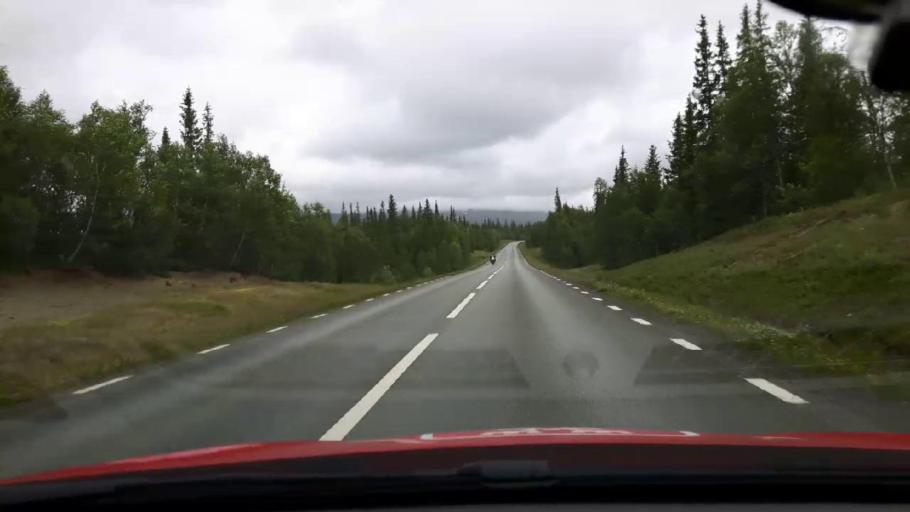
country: NO
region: Nord-Trondelag
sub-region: Meraker
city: Meraker
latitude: 63.2664
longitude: 12.1607
